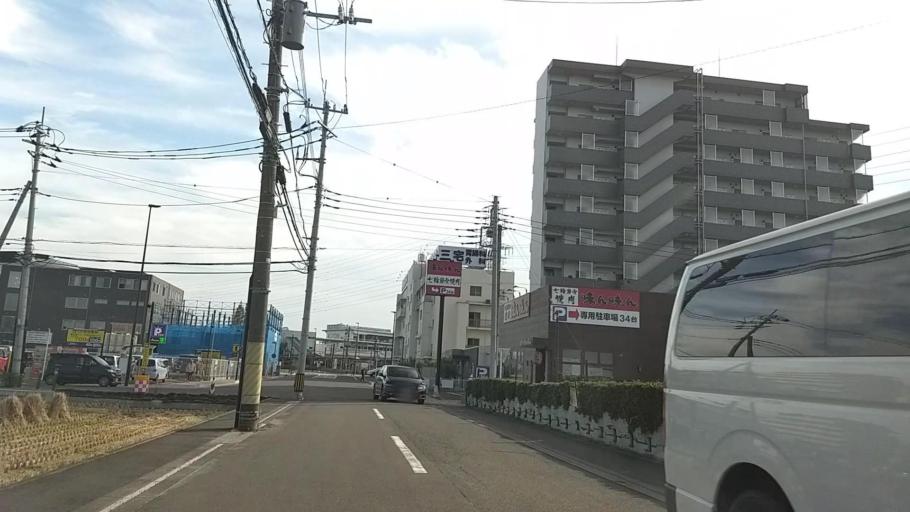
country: JP
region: Kanagawa
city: Atsugi
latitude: 35.4539
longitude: 139.3865
